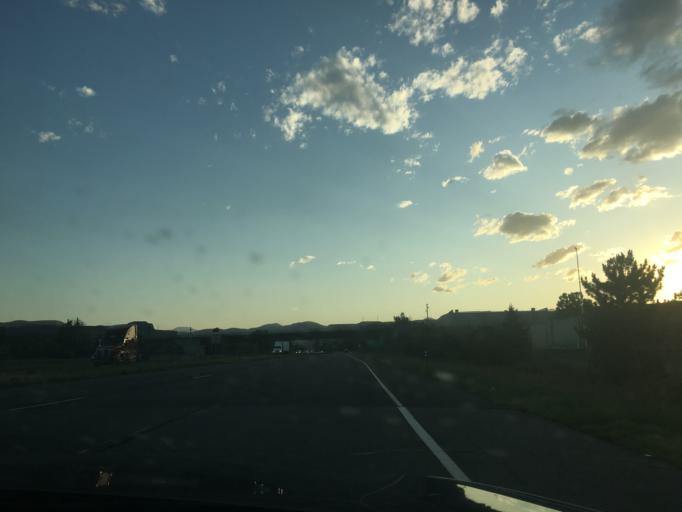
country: US
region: Colorado
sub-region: Jefferson County
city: Applewood
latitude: 39.7752
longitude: -105.1535
